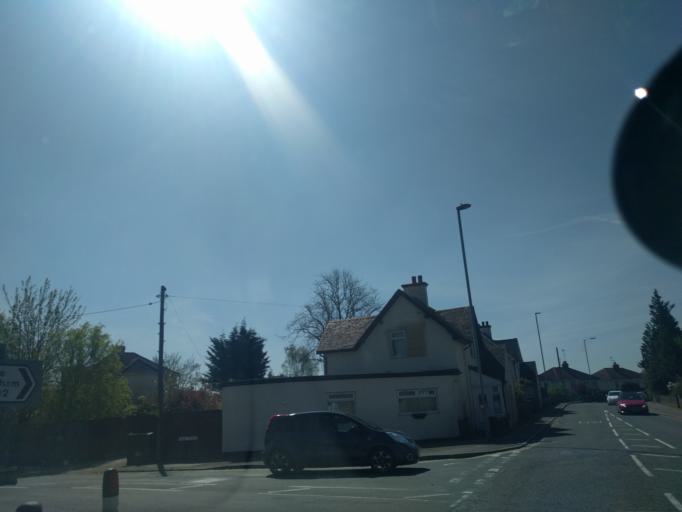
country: GB
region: England
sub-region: Wiltshire
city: Royal Wootton Bassett
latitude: 51.5385
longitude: -1.9080
